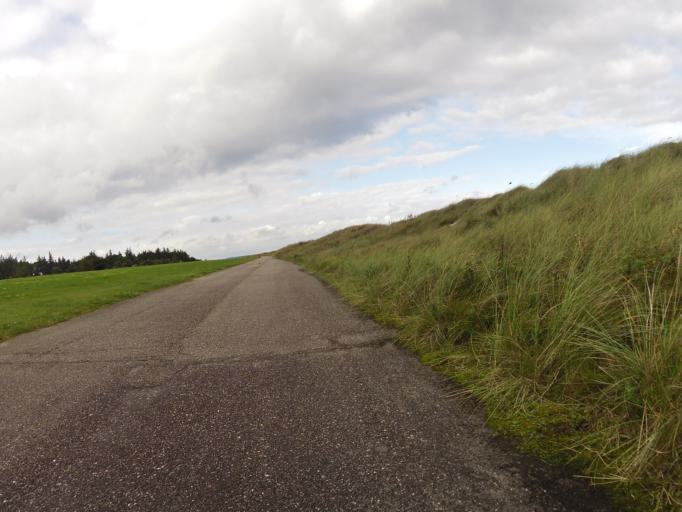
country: DE
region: Schleswig-Holstein
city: Wisch
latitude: 54.4332
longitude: 10.3463
